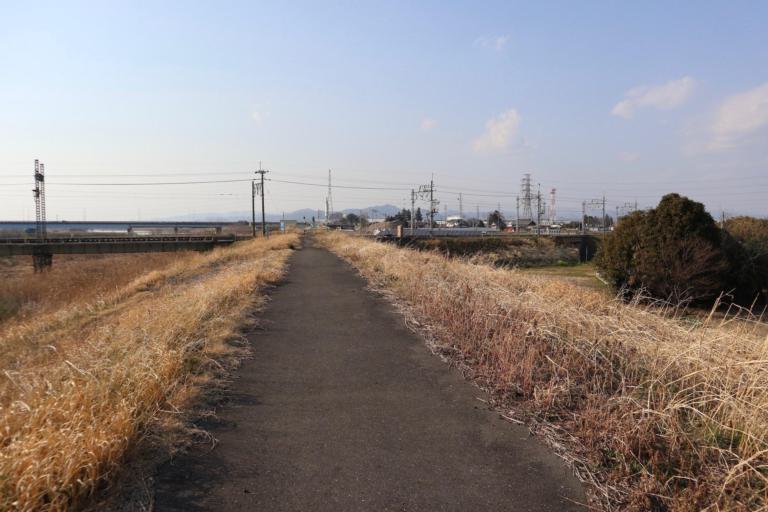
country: JP
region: Gunma
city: Tatebayashi
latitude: 36.2727
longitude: 139.5574
